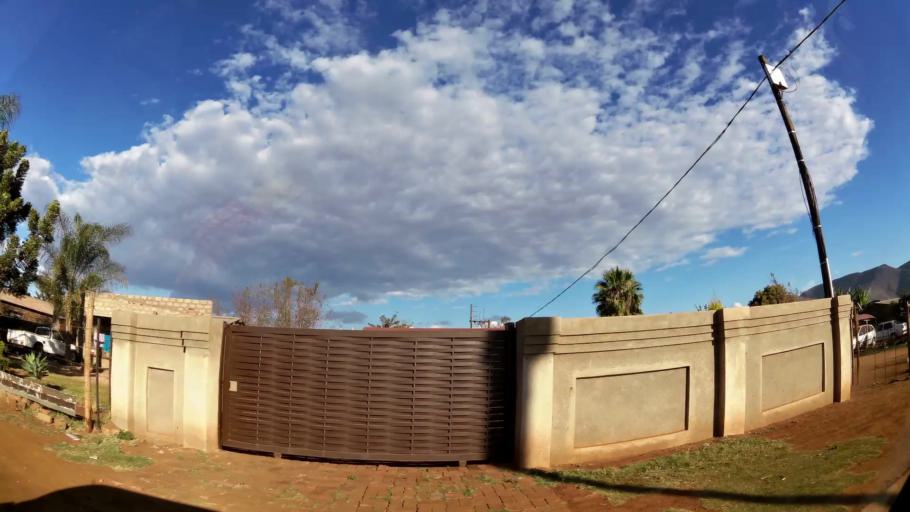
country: ZA
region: Limpopo
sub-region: Waterberg District Municipality
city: Mokopane
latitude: -24.1870
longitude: 28.9758
